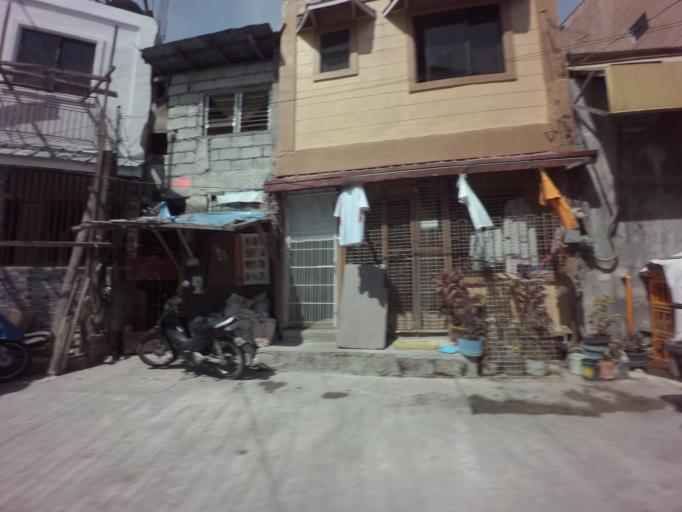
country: PH
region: Calabarzon
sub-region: Province of Rizal
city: Pateros
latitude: 14.5335
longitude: 121.0745
